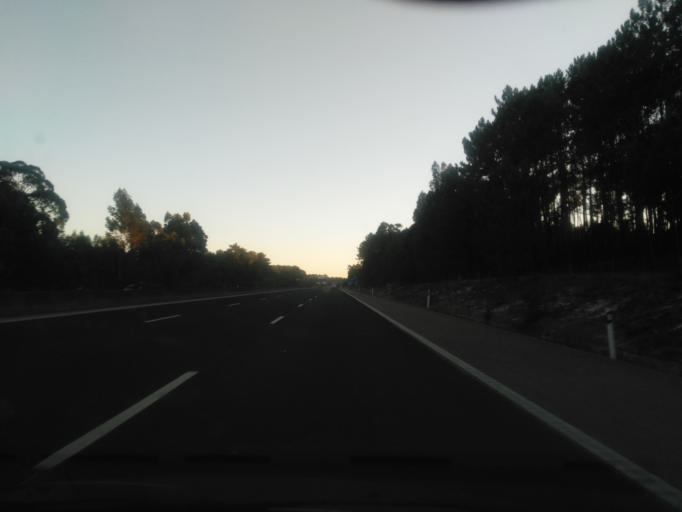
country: PT
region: Leiria
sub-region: Leiria
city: Maceira
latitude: 39.7077
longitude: -8.9186
